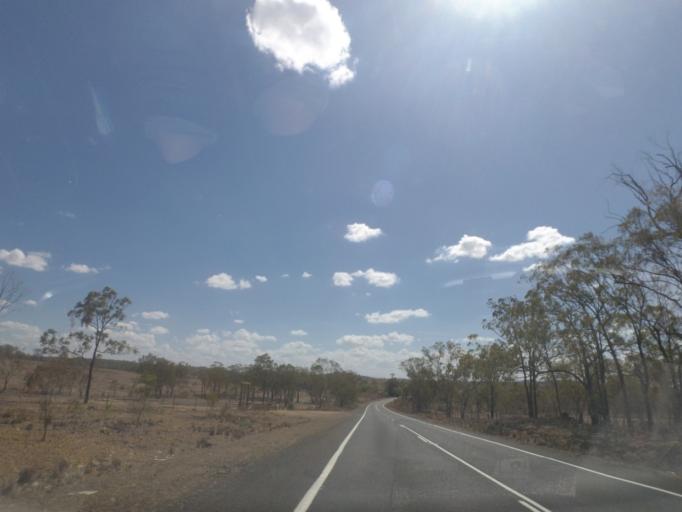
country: AU
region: Queensland
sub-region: Southern Downs
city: Warwick
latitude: -28.2050
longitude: 151.5855
